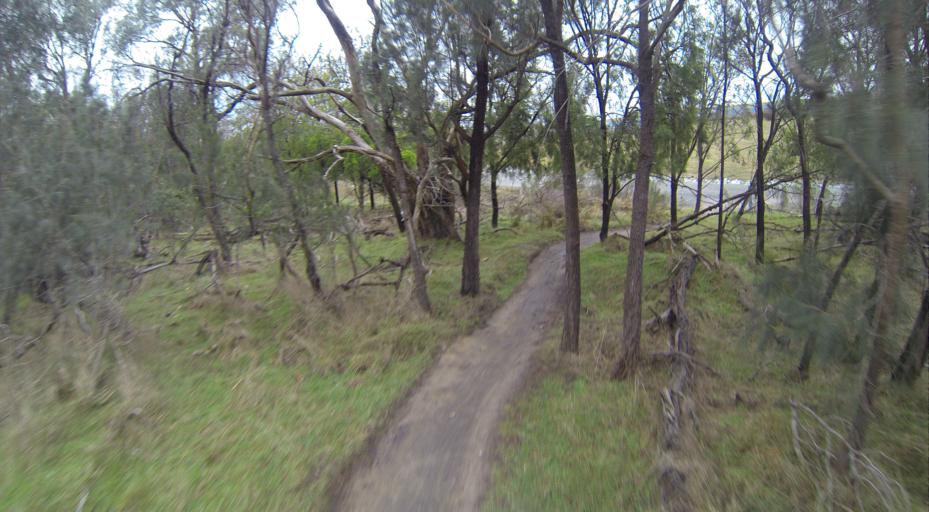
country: AU
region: Victoria
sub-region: Casey
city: Narre Warren North
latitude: -37.9712
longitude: 145.2954
